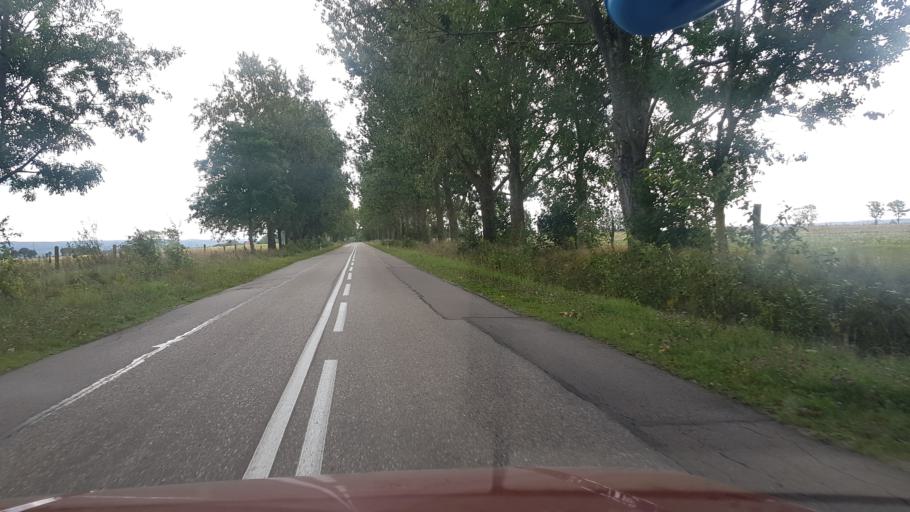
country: PL
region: Pomeranian Voivodeship
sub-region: Powiat slupski
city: Kepice
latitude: 54.0888
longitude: 16.8431
